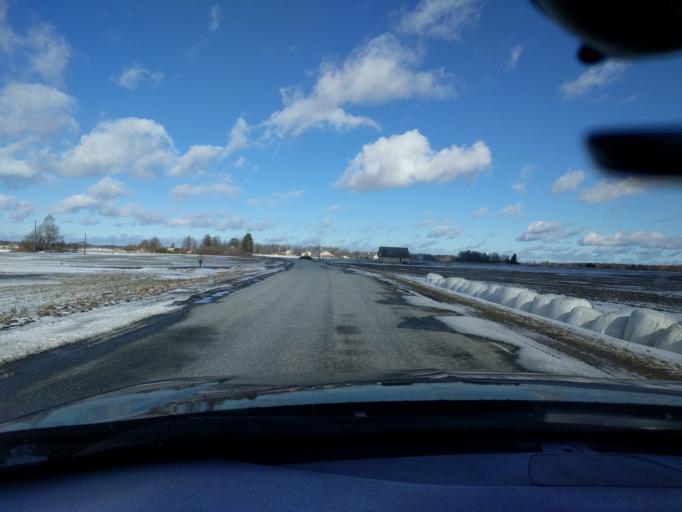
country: EE
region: Harju
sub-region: Raasiku vald
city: Raasiku
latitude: 59.3266
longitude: 25.1601
